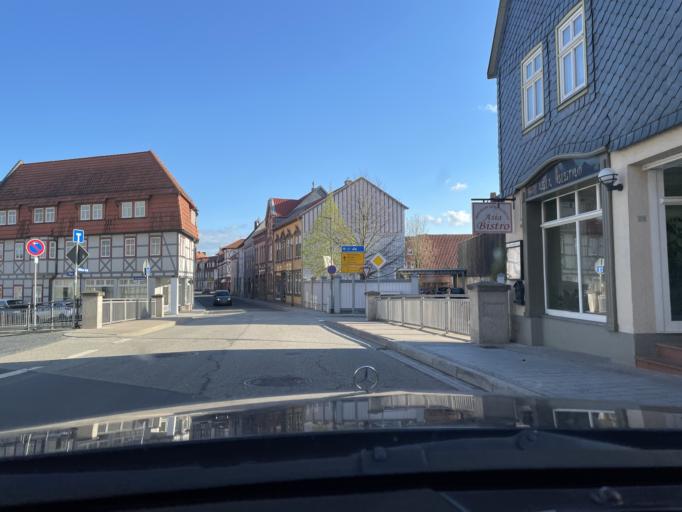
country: DE
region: Thuringia
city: Dingelstadt
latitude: 51.3144
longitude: 10.3192
